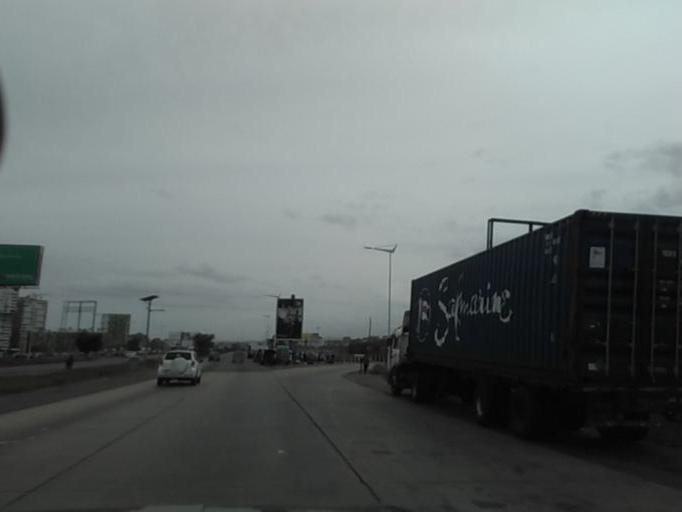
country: GH
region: Greater Accra
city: Medina Estates
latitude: 5.6243
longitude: -0.1729
